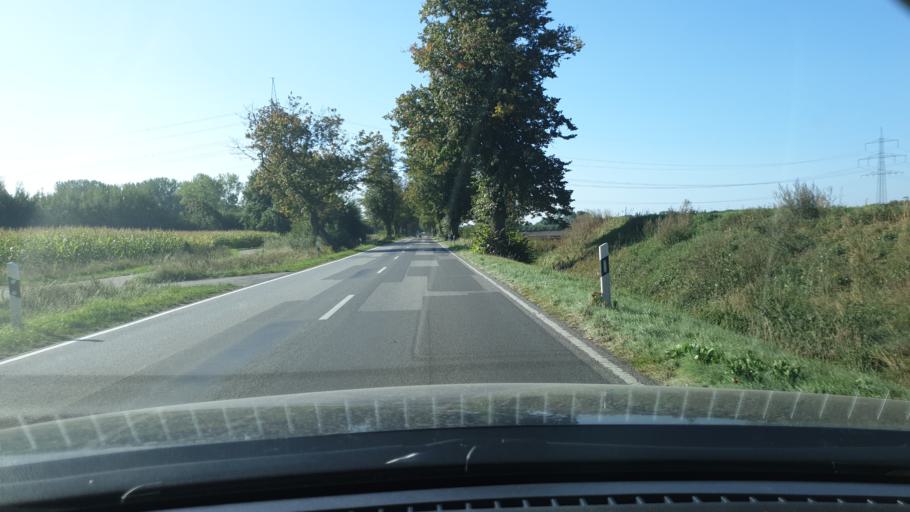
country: DE
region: Mecklenburg-Vorpommern
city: Wittenburg
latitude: 53.5258
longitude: 11.0736
